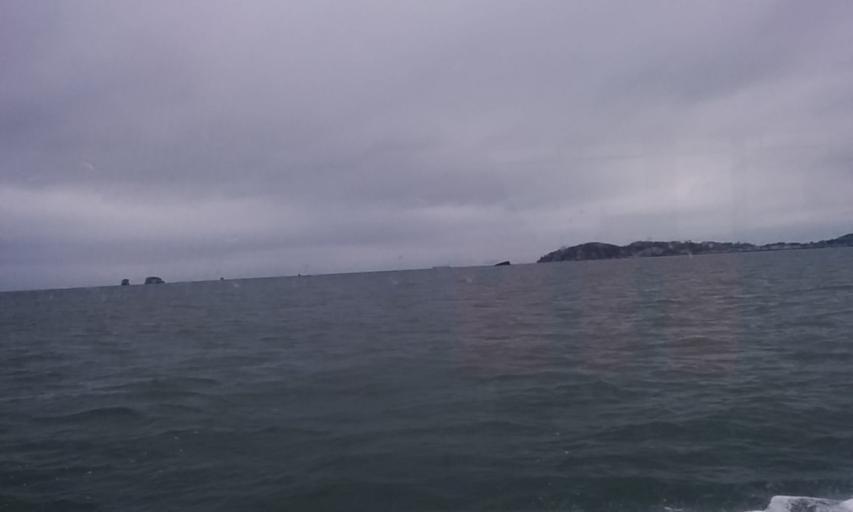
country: JP
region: Miyagi
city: Matsushima
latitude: 38.3235
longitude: 141.0930
